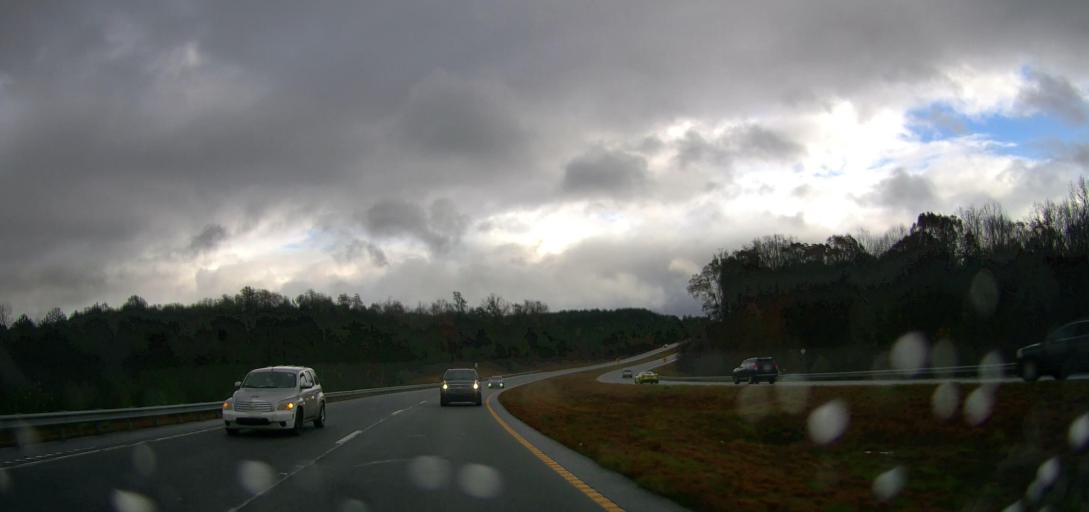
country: US
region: Georgia
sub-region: Jackson County
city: Nicholson
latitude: 34.0594
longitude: -83.4147
